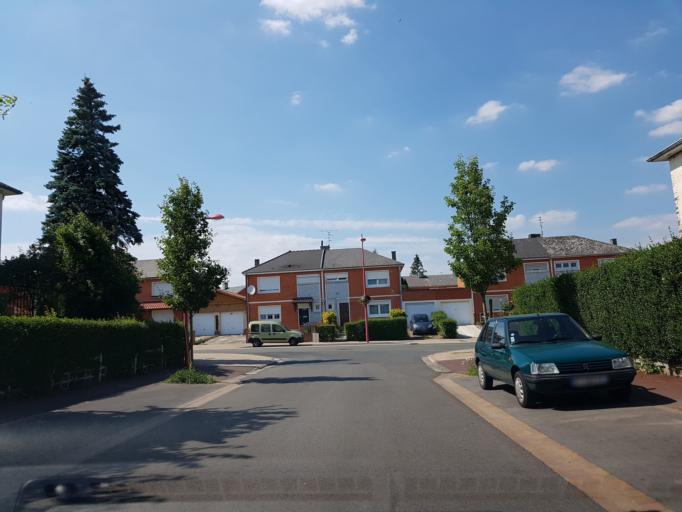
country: FR
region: Nord-Pas-de-Calais
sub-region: Departement du Nord
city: Roeulx
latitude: 50.3086
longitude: 3.3313
